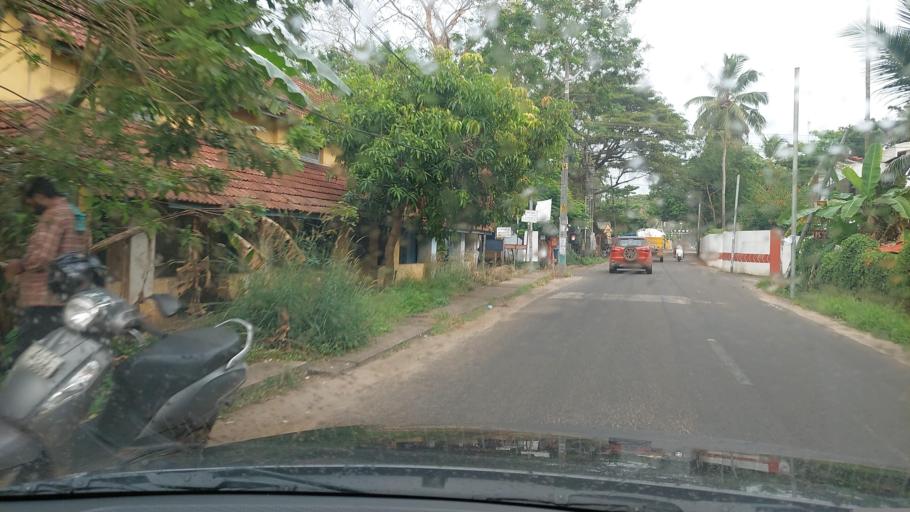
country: IN
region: Kerala
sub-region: Kozhikode
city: Kozhikode
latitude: 11.2915
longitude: 75.7606
